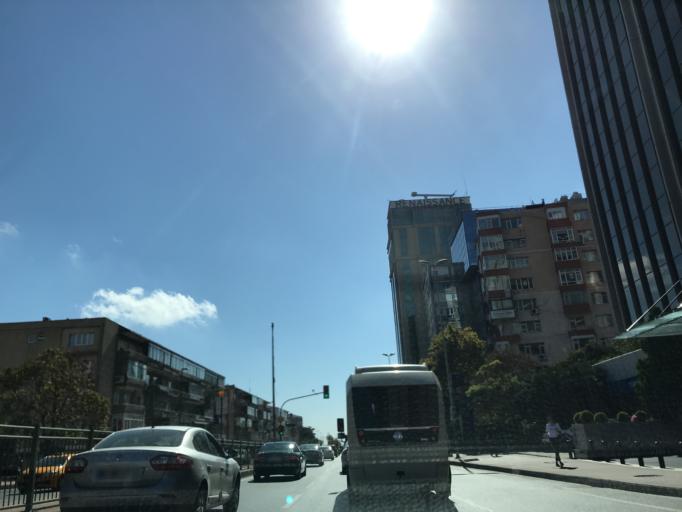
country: TR
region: Istanbul
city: Sisli
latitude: 41.0609
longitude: 29.0110
